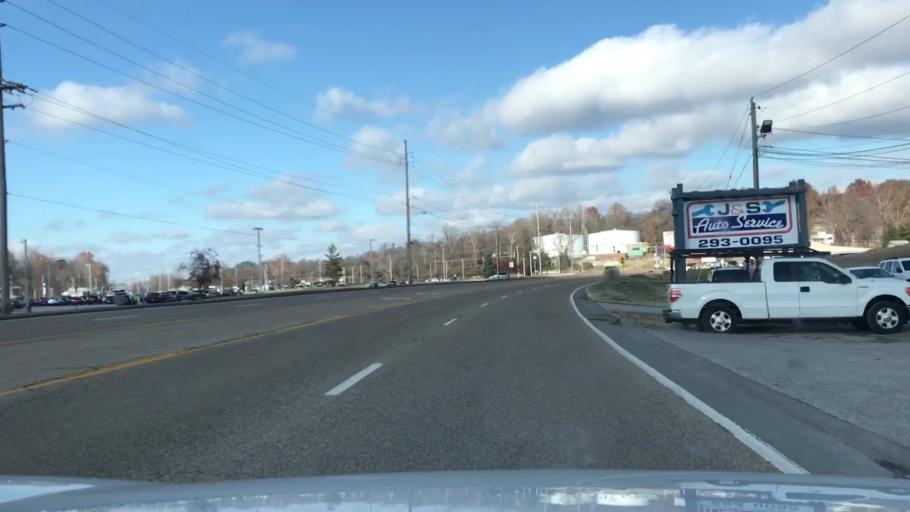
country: US
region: Illinois
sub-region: Saint Clair County
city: Caseyville
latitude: 38.5919
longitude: -90.0456
